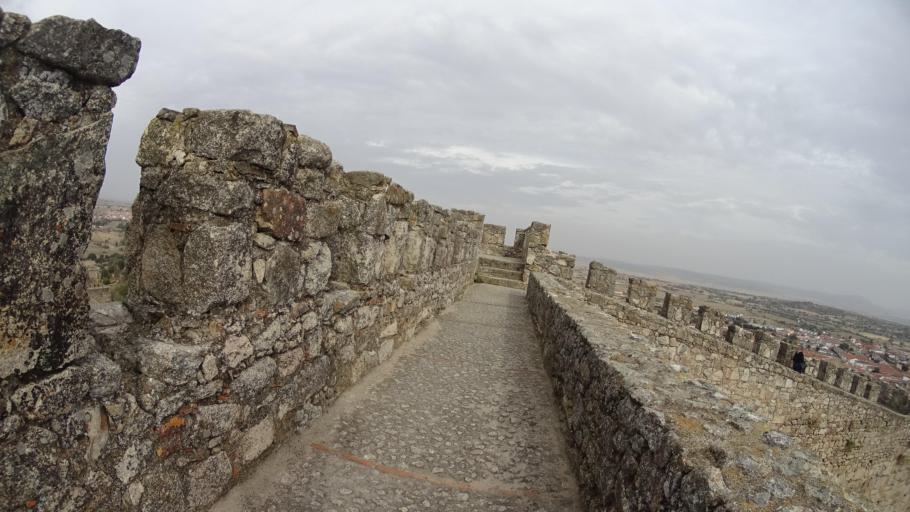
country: ES
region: Extremadura
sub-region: Provincia de Caceres
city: Trujillo
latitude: 39.4626
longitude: -5.8827
